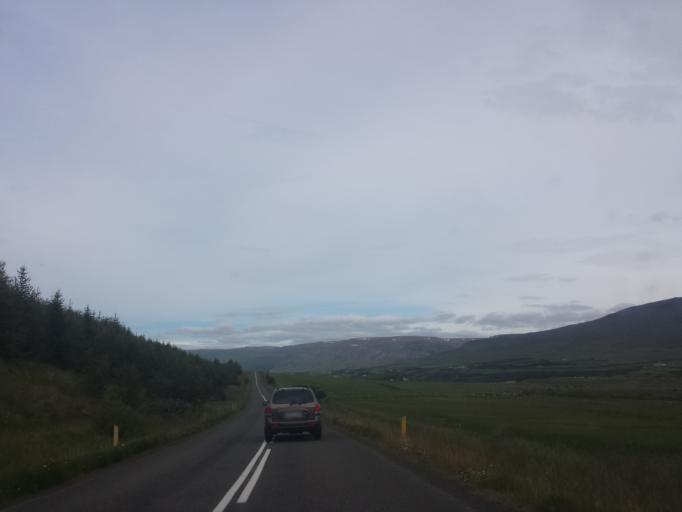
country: IS
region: Northeast
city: Akureyri
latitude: 65.5416
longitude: -18.1233
